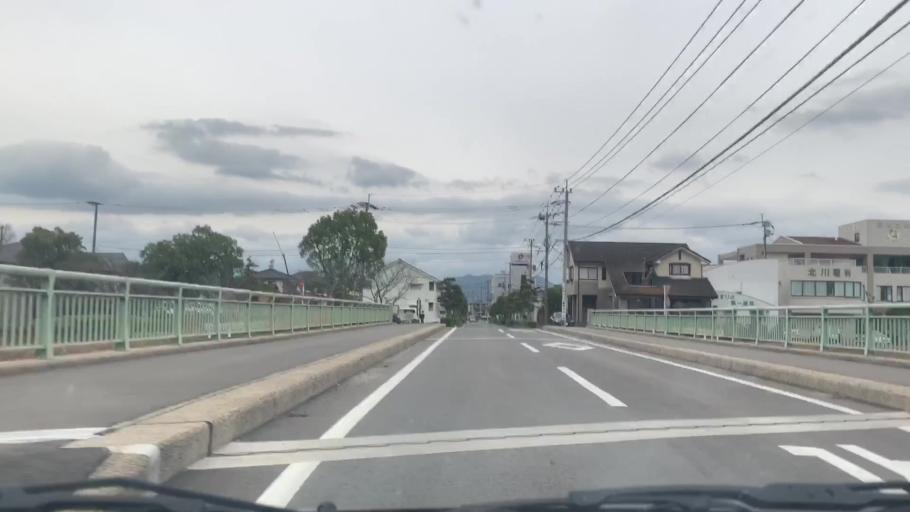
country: JP
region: Saga Prefecture
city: Takeocho-takeo
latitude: 33.1908
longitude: 130.0252
